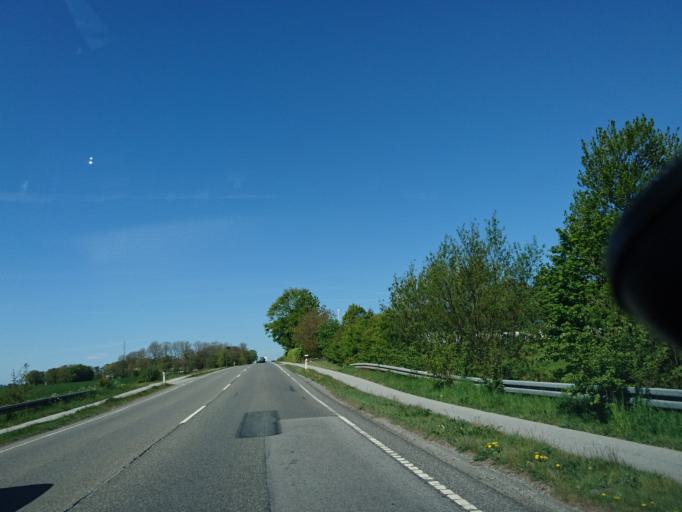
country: DK
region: North Denmark
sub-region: Hjorring Kommune
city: Tars
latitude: 57.4555
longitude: 10.1053
